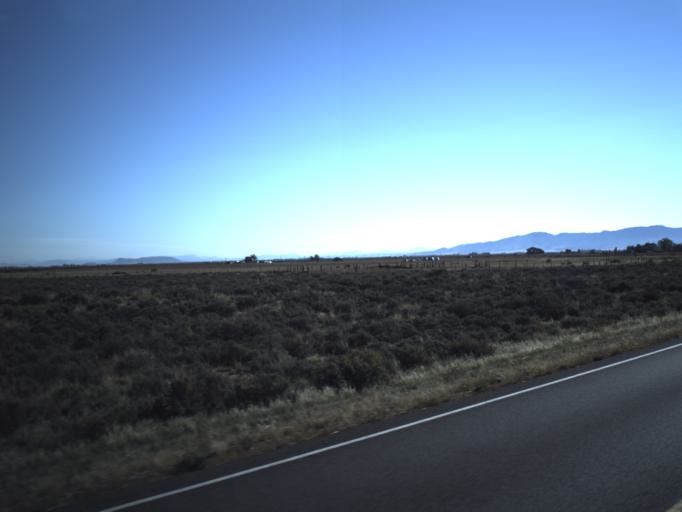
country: US
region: Utah
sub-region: Washington County
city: Enterprise
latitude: 37.7471
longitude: -113.7614
